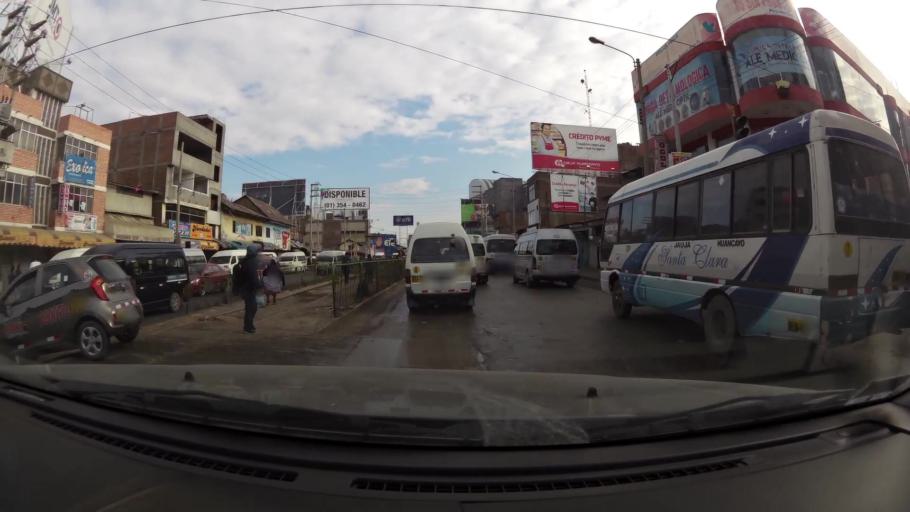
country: PE
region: Junin
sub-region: Provincia de Huancayo
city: Huancayo
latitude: -12.0699
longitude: -75.2048
